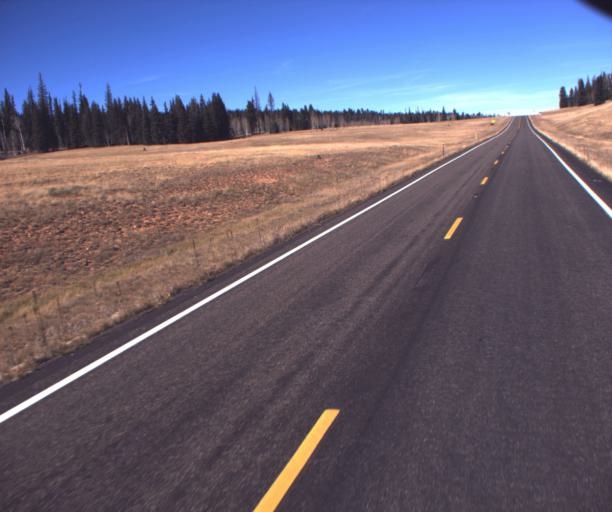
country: US
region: Arizona
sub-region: Coconino County
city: Grand Canyon
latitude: 36.4059
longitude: -112.1306
